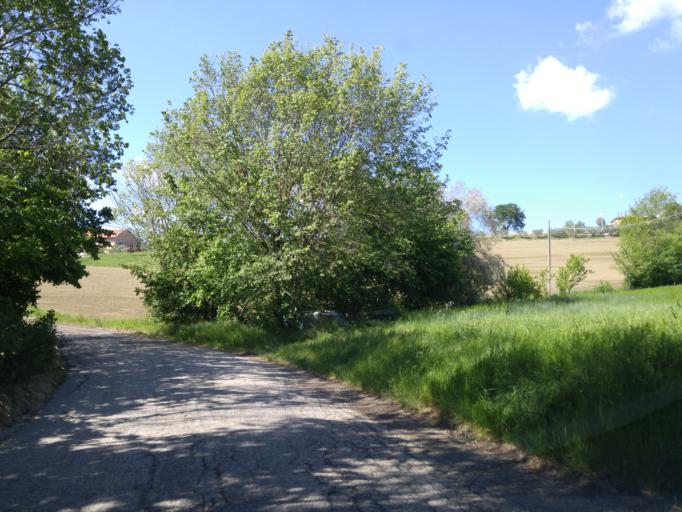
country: IT
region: The Marches
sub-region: Provincia di Pesaro e Urbino
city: Cartoceto
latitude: 43.7842
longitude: 12.9073
